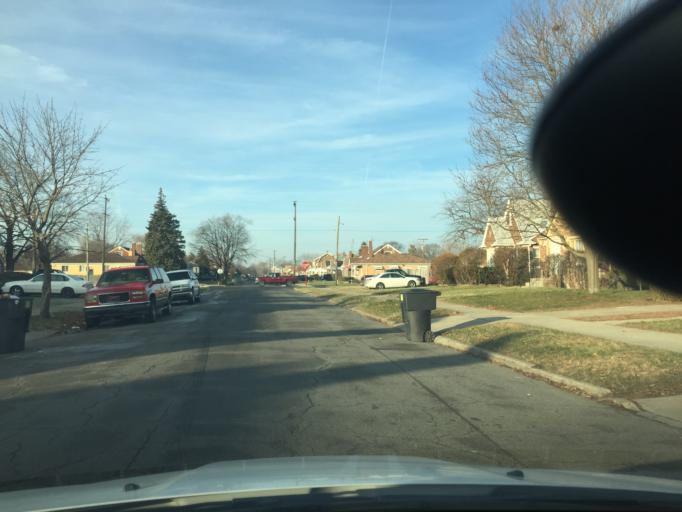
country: US
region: Michigan
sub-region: Macomb County
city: Eastpointe
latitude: 42.4446
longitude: -82.9649
